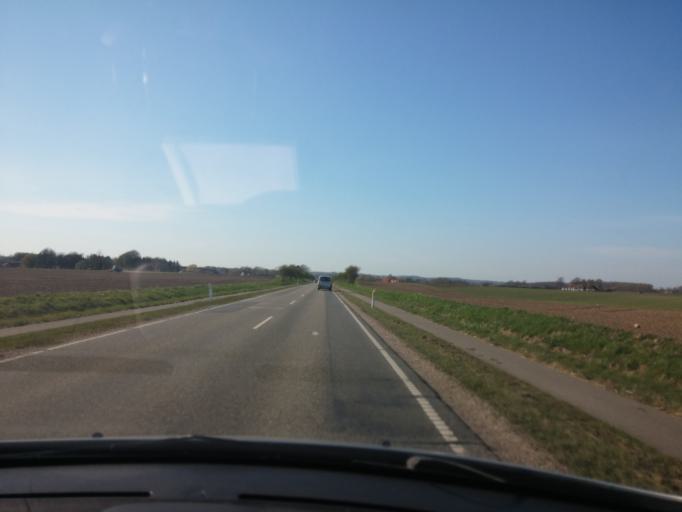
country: DK
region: Central Jutland
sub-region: Odder Kommune
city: Odder
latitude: 55.9520
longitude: 10.1990
